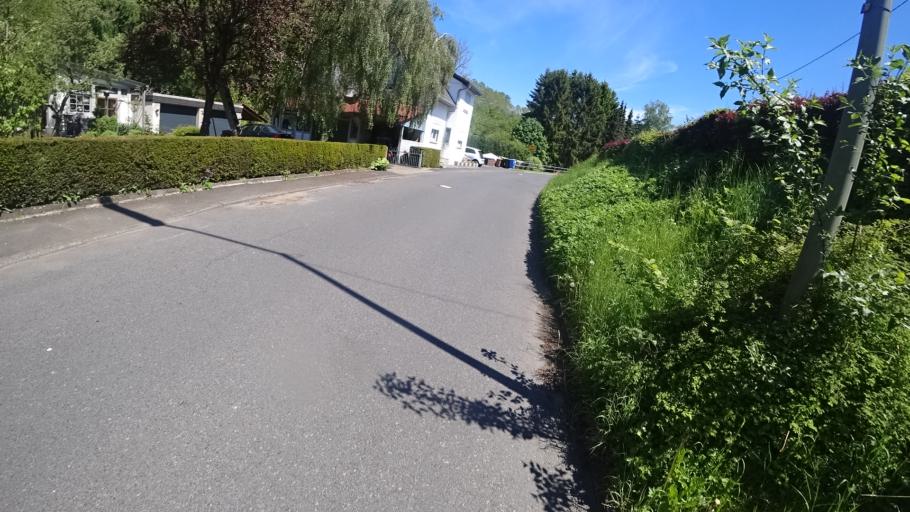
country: DE
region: Rheinland-Pfalz
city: Elben
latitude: 50.7501
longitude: 7.8360
